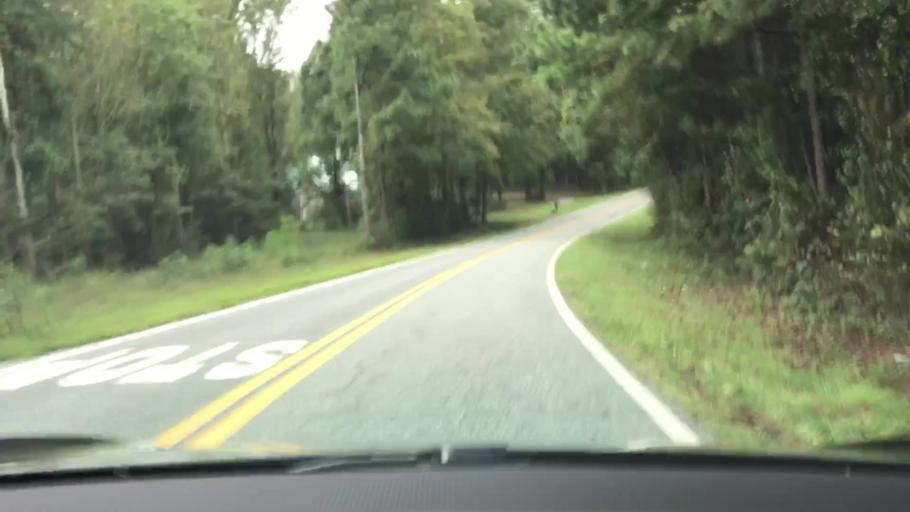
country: US
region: Georgia
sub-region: Barrow County
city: Auburn
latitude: 34.0280
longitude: -83.7763
